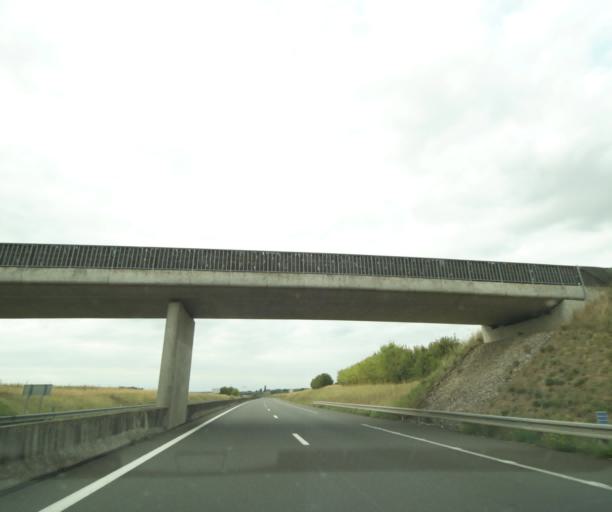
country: FR
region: Centre
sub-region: Departement d'Indre-et-Loire
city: Parcay-Meslay
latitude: 47.4695
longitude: 0.7604
